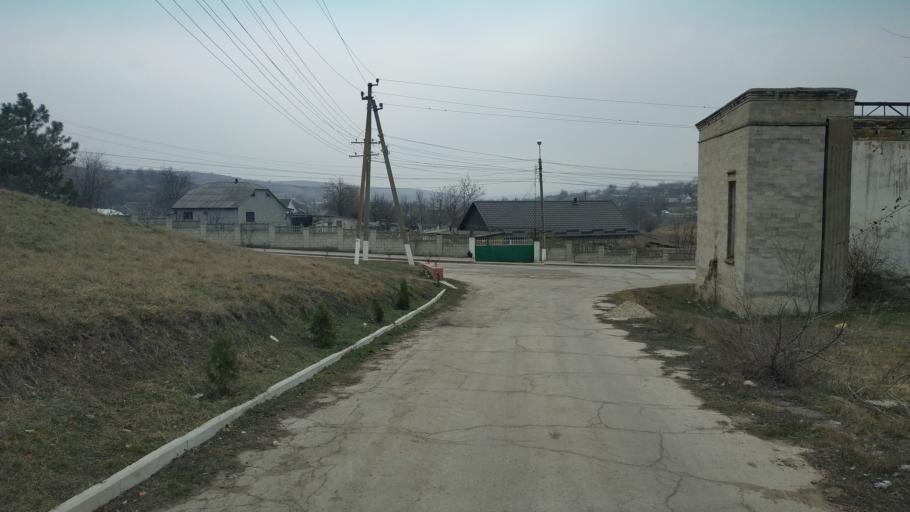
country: MD
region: Chisinau
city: Singera
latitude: 46.8235
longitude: 29.0392
